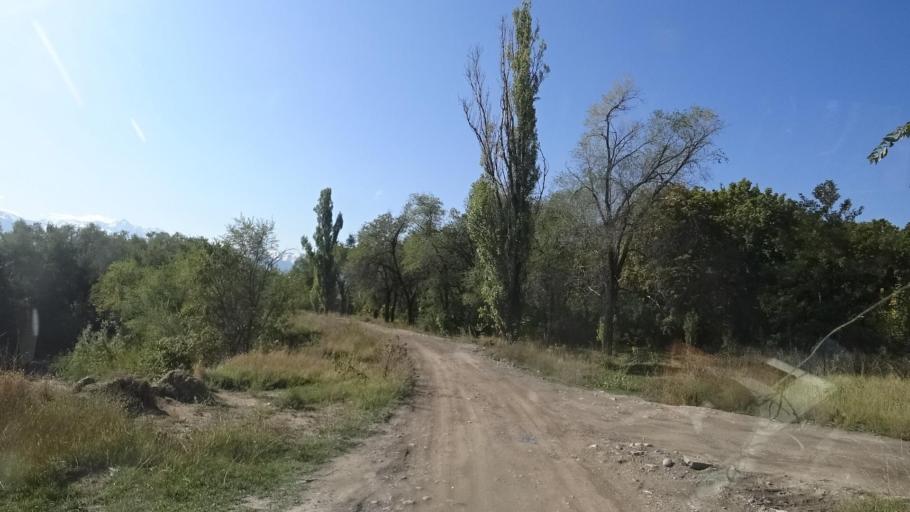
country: KZ
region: Almaty Oblysy
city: Pervomayskiy
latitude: 43.3314
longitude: 76.9998
